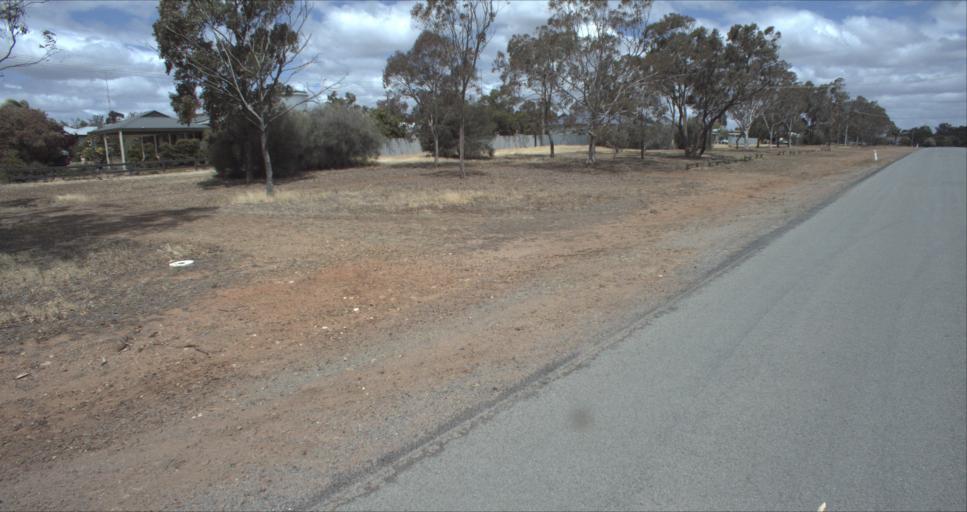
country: AU
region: New South Wales
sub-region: Leeton
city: Leeton
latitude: -34.5588
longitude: 146.3953
